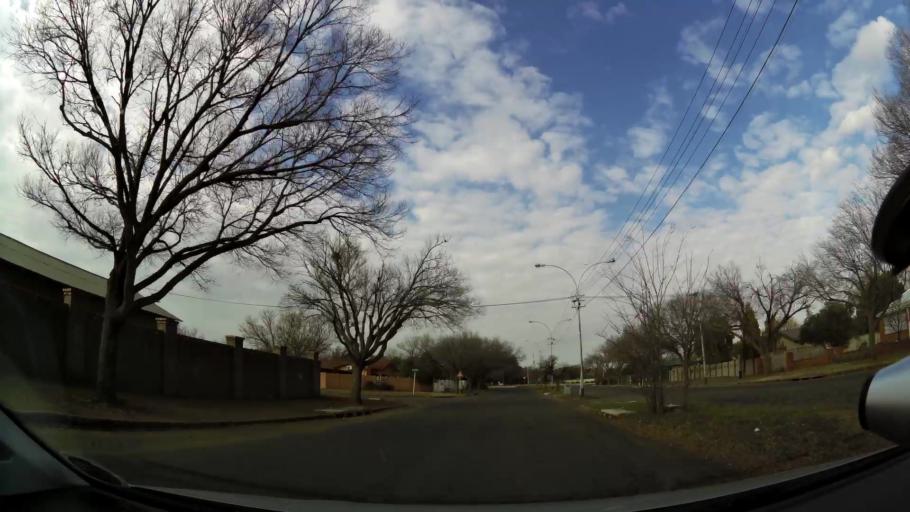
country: ZA
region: Orange Free State
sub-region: Mangaung Metropolitan Municipality
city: Bloemfontein
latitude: -29.0799
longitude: 26.2433
